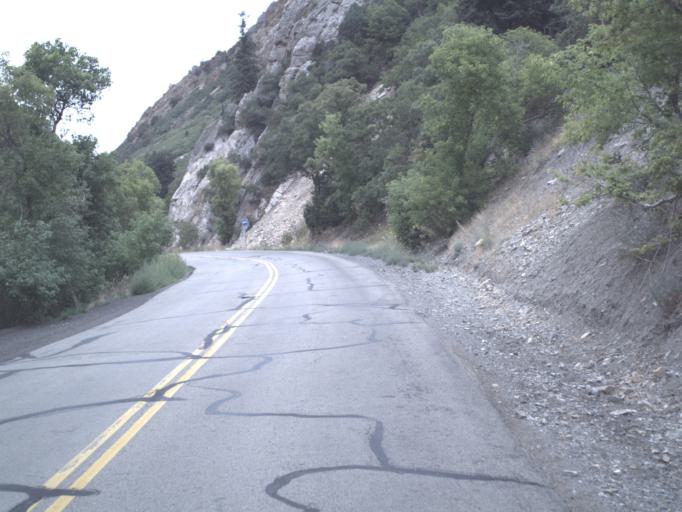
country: US
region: Utah
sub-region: Utah County
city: Cedar Hills
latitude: 40.4411
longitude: -111.7162
